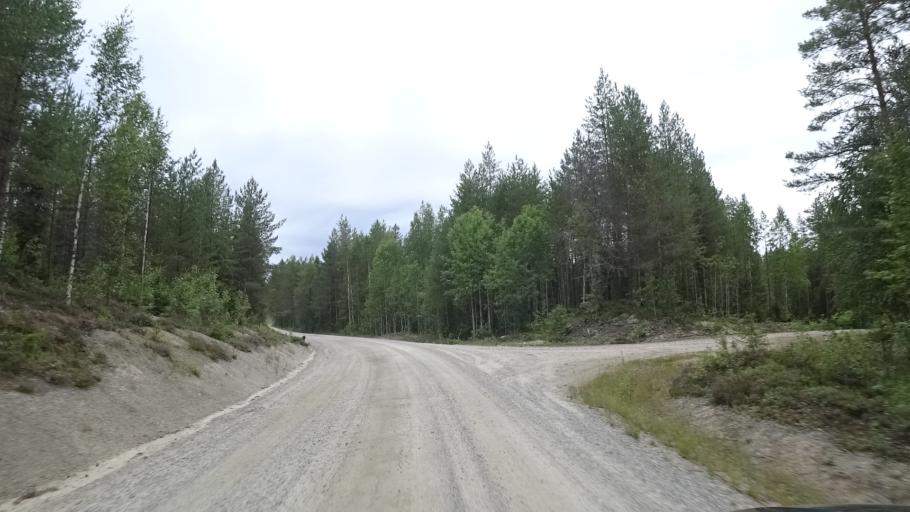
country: FI
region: North Karelia
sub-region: Pielisen Karjala
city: Lieksa
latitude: 63.2406
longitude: 30.3501
